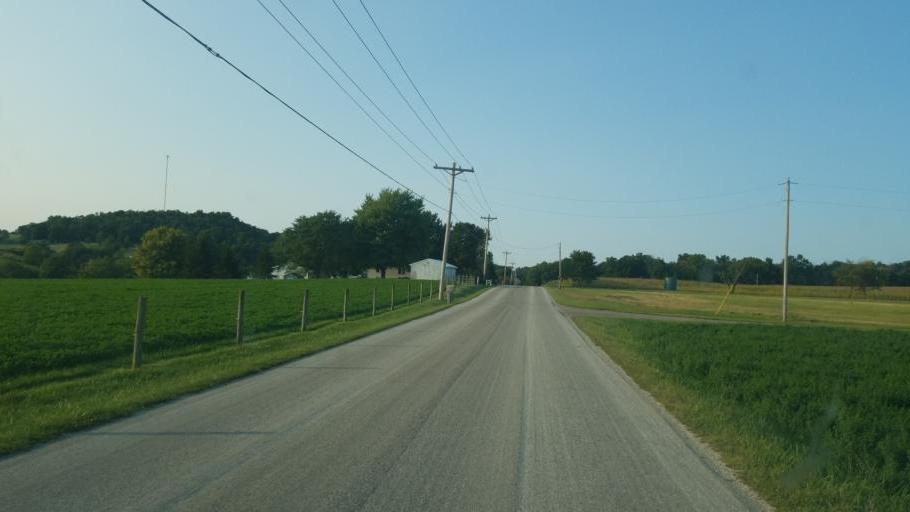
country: US
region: Ohio
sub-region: Wayne County
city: Shreve
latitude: 40.6629
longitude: -81.9238
